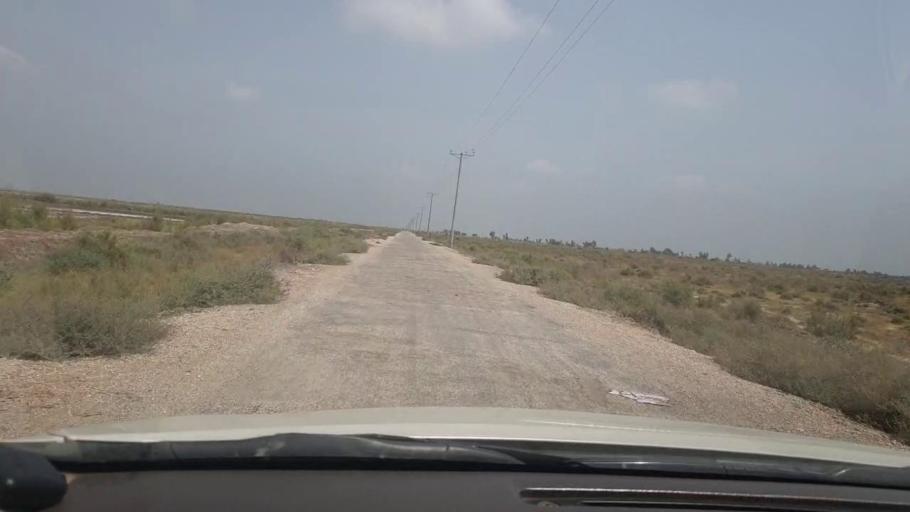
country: PK
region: Sindh
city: Garhi Yasin
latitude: 27.9871
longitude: 68.5018
